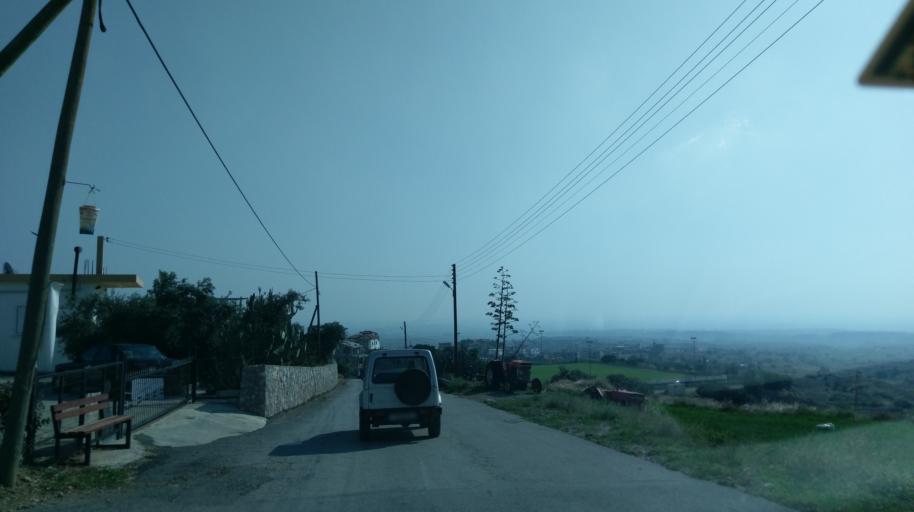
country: CY
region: Ammochostos
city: Lefkonoiko
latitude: 35.2798
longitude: 33.5750
